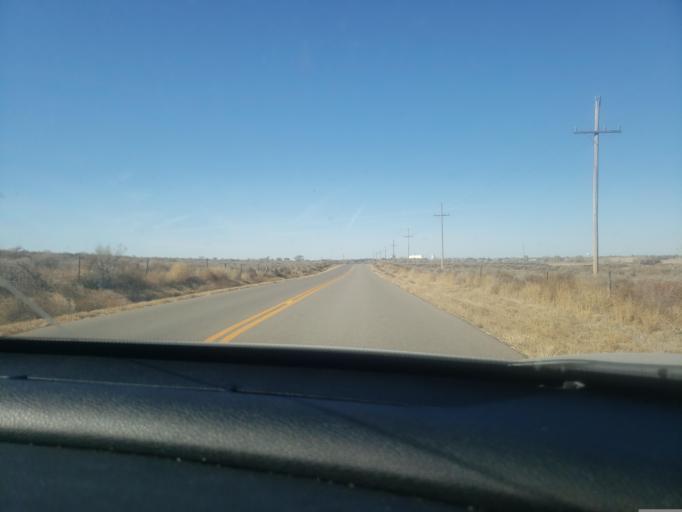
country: US
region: Kansas
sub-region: Finney County
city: Garden City
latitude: 37.9482
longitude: -100.8502
